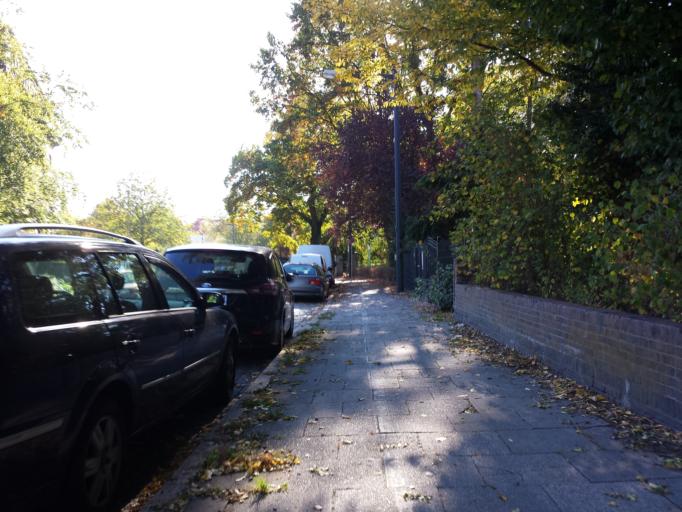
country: DE
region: Bremen
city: Bremen
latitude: 53.1051
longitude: 8.7765
